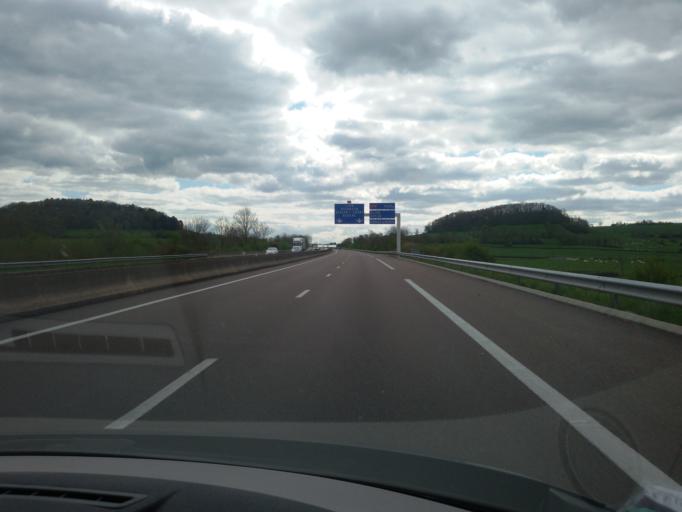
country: FR
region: Bourgogne
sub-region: Departement de la Cote-d'Or
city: Pouilly-en-Auxois
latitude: 47.2565
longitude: 4.5343
